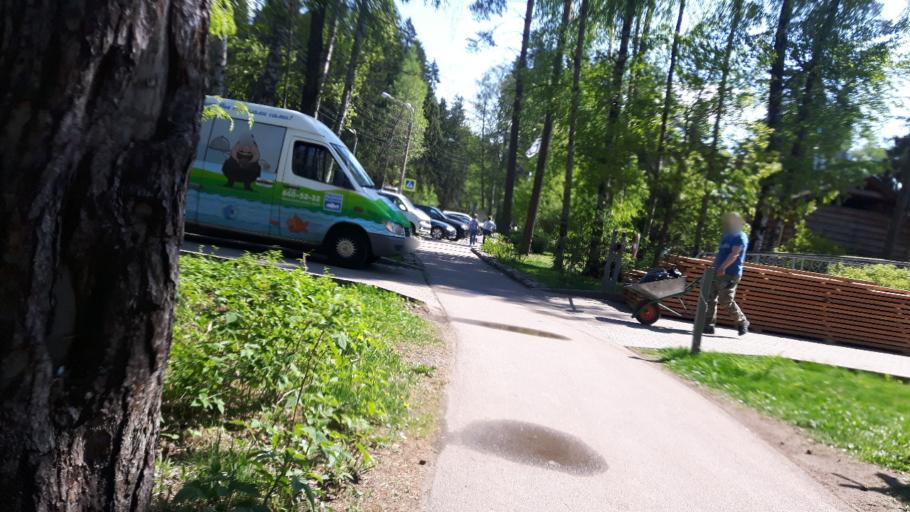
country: RU
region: St.-Petersburg
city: Komarovo
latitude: 60.1712
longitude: 29.8128
